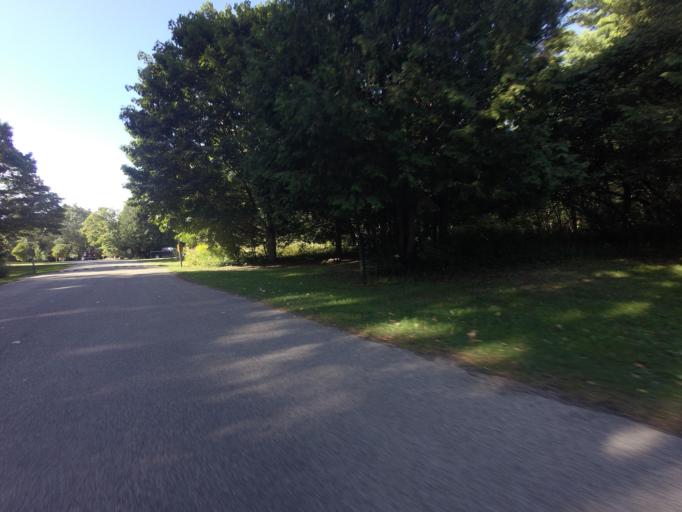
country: CA
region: Ontario
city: Waterloo
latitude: 43.6696
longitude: -80.4500
